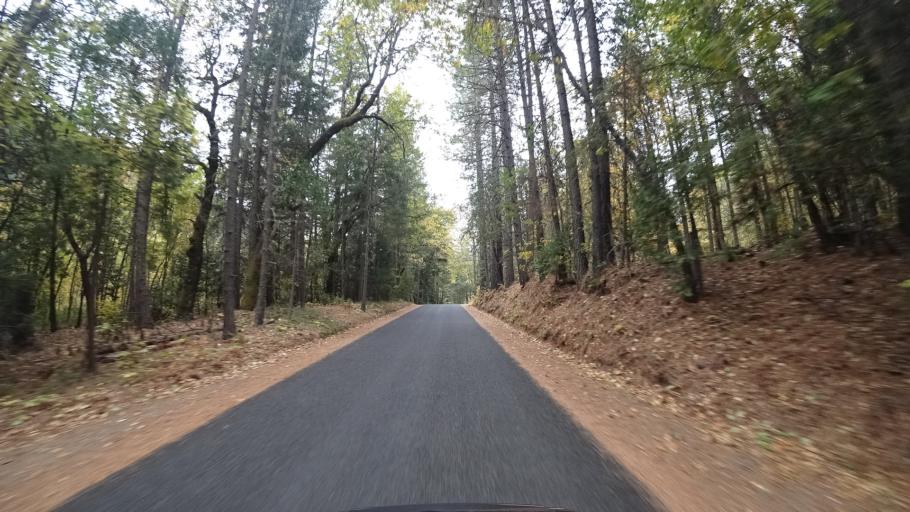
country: US
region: California
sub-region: Siskiyou County
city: Happy Camp
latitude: 41.8518
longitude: -123.1744
